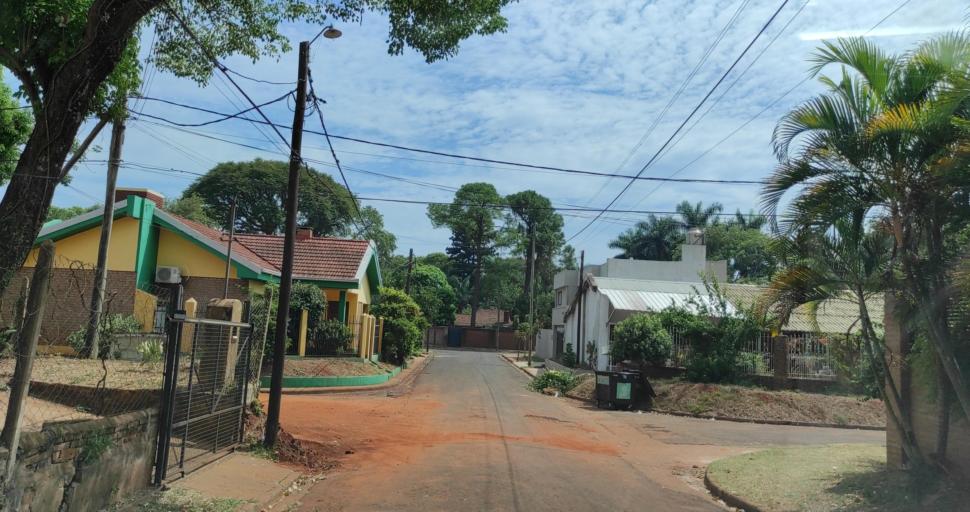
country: AR
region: Misiones
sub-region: Departamento de Capital
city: Posadas
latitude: -27.3679
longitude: -55.9218
